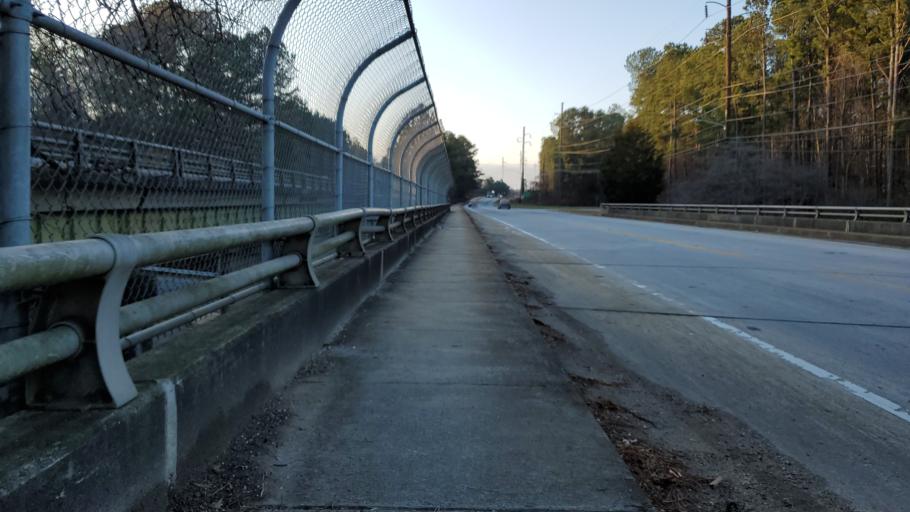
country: US
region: Georgia
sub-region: DeKalb County
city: Stone Mountain
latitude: 33.8140
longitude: -84.1772
